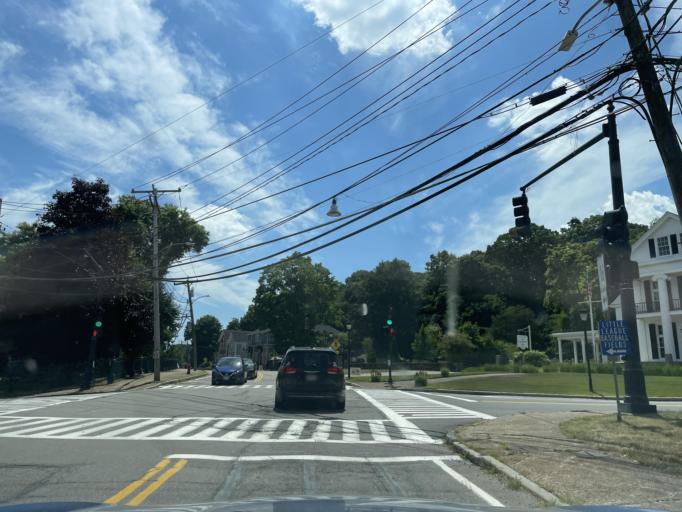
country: US
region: Massachusetts
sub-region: Norfolk County
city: Wellesley
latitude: 42.2730
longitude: -71.3160
